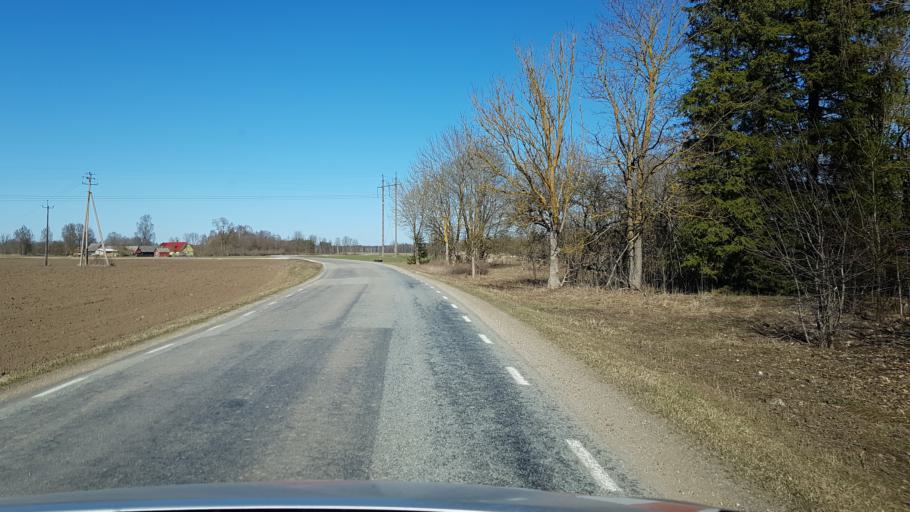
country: EE
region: Laeaene-Virumaa
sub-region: Someru vald
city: Someru
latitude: 59.3731
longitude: 26.4525
